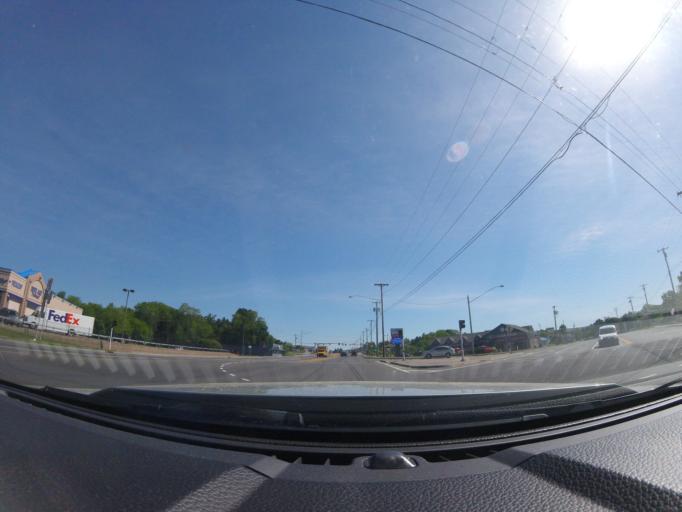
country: US
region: New York
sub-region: Cortland County
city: Munsons Corners
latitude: 42.5978
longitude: -76.2047
